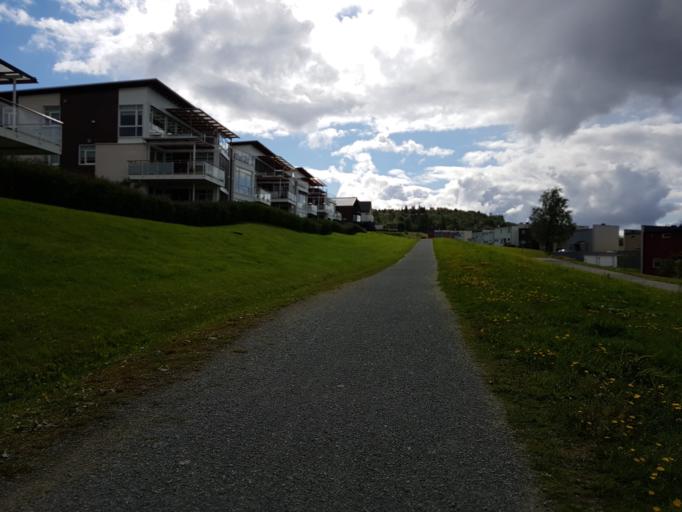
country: NO
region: Sor-Trondelag
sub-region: Trondheim
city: Trondheim
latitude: 63.4146
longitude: 10.4651
